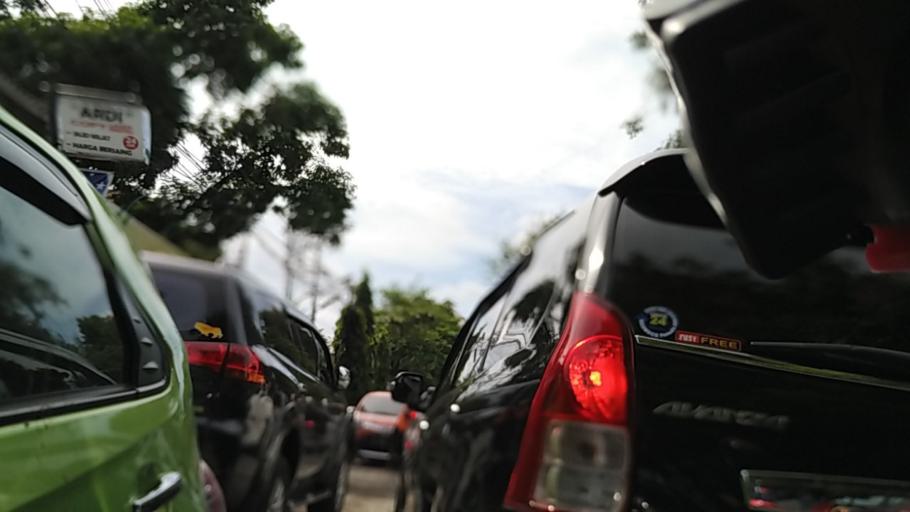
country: ID
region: Central Java
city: Semarang
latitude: -6.9963
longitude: 110.4261
